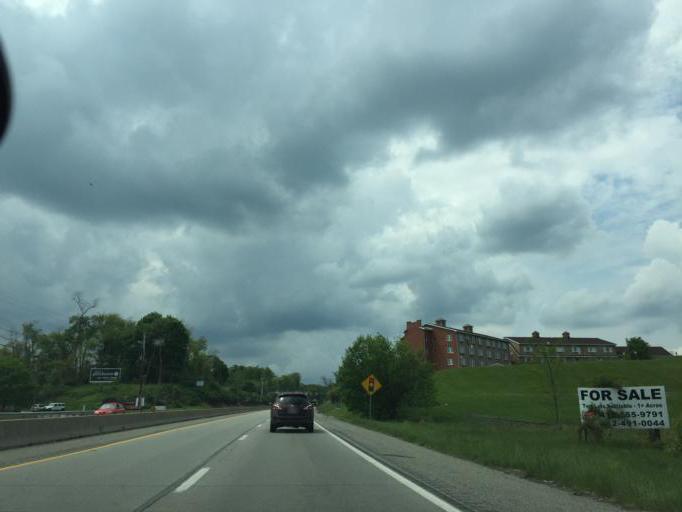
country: US
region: Pennsylvania
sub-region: Westmoreland County
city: Lawson Heights
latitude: 40.2895
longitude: -79.4606
